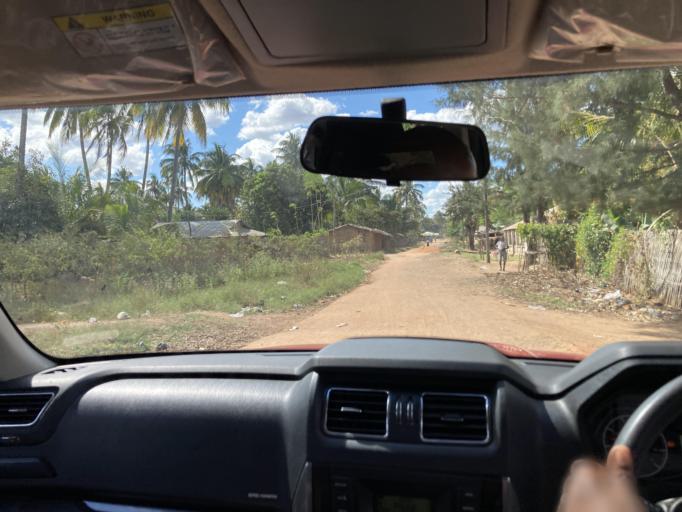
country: MZ
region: Cabo Delgado
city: Montepuez
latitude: -13.1392
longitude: 39.0005
